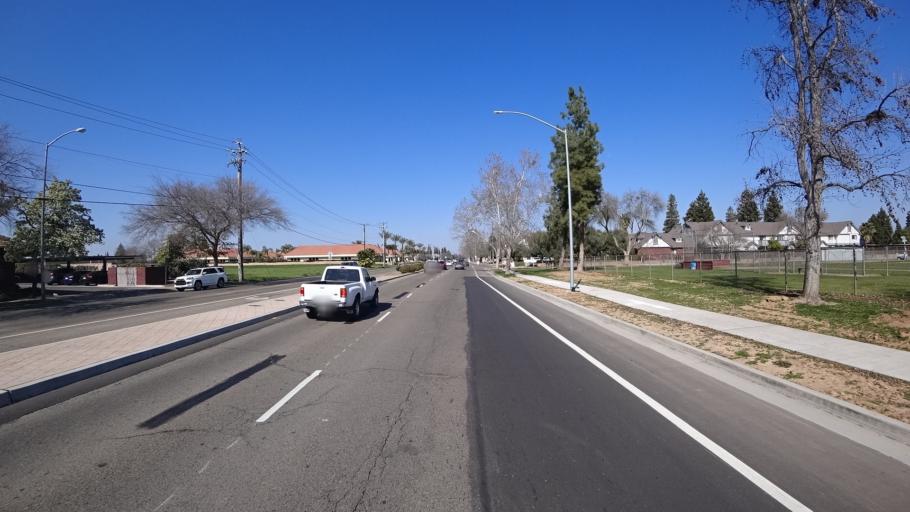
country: US
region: California
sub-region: Fresno County
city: Clovis
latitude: 36.8417
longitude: -119.7566
